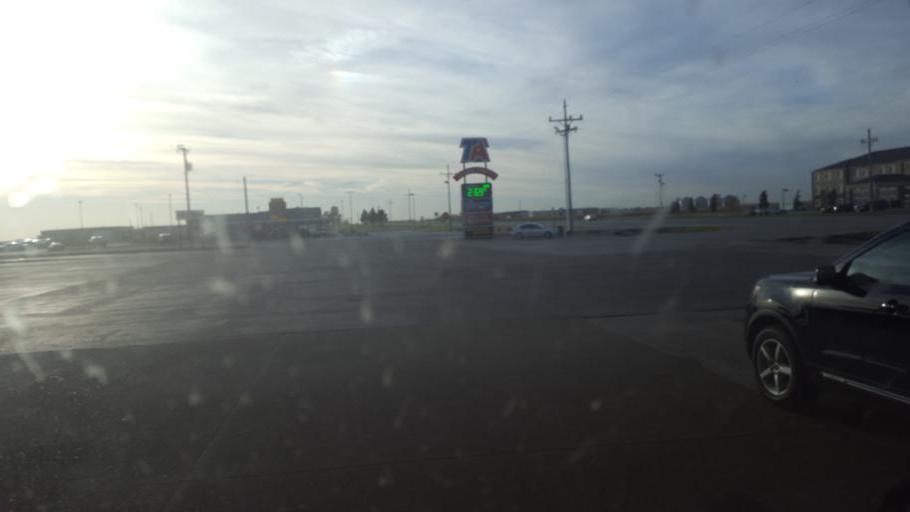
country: US
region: Kansas
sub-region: Logan County
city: Oakley
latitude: 39.1190
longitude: -100.8112
